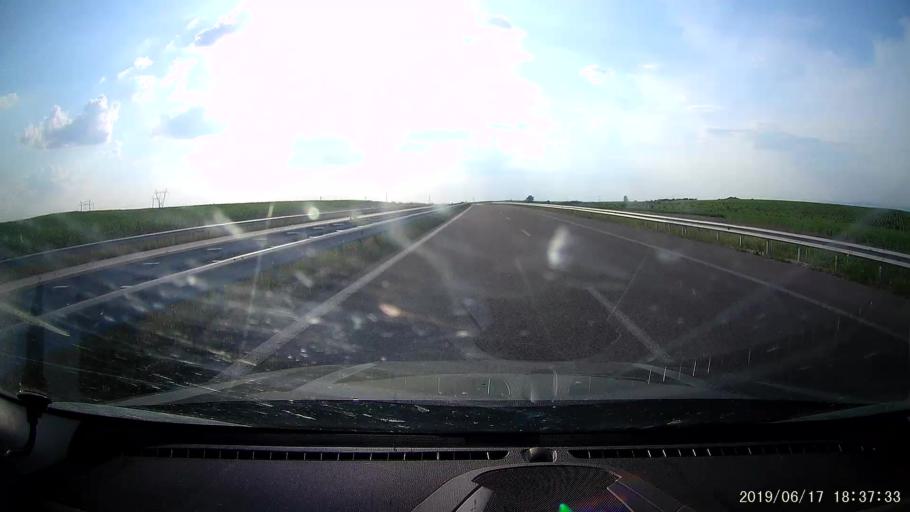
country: BG
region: Stara Zagora
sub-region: Obshtina Chirpan
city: Chirpan
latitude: 42.1315
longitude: 25.3580
